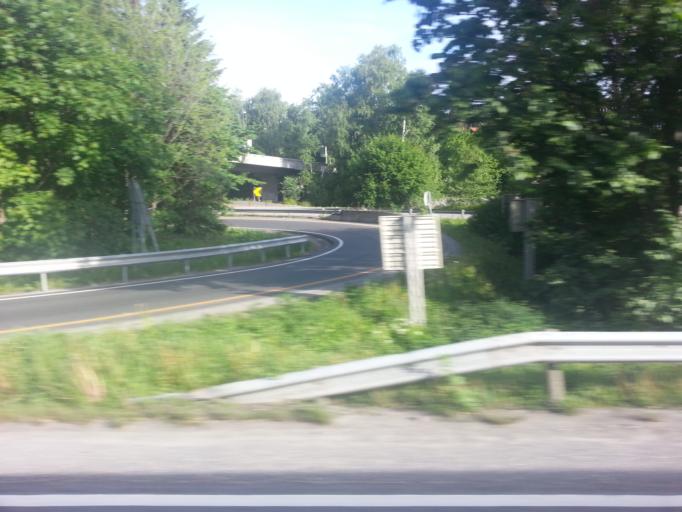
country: NO
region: Akershus
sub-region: Baerum
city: Lysaker
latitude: 59.9103
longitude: 10.6290
